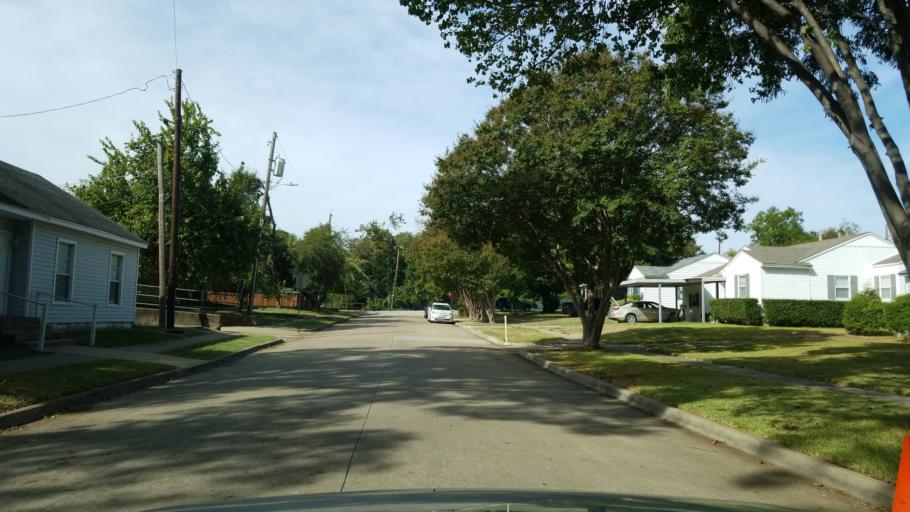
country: US
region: Texas
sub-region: Dallas County
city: Garland
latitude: 32.9046
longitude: -96.6520
